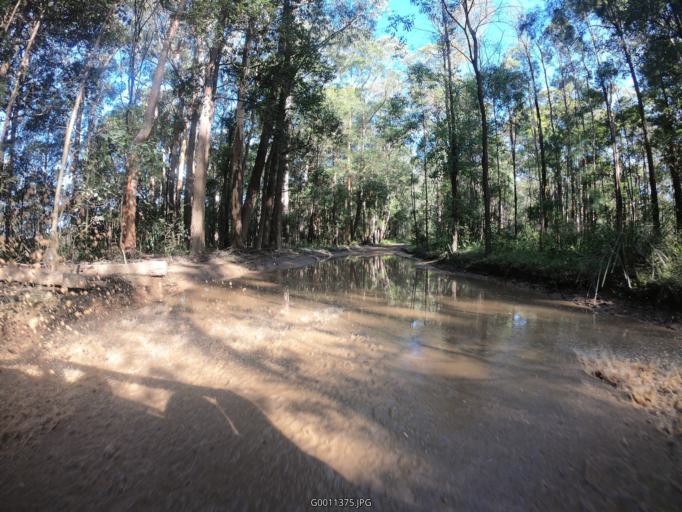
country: AU
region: New South Wales
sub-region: Lake Macquarie Shire
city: Cooranbong
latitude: -33.0255
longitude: 151.3022
